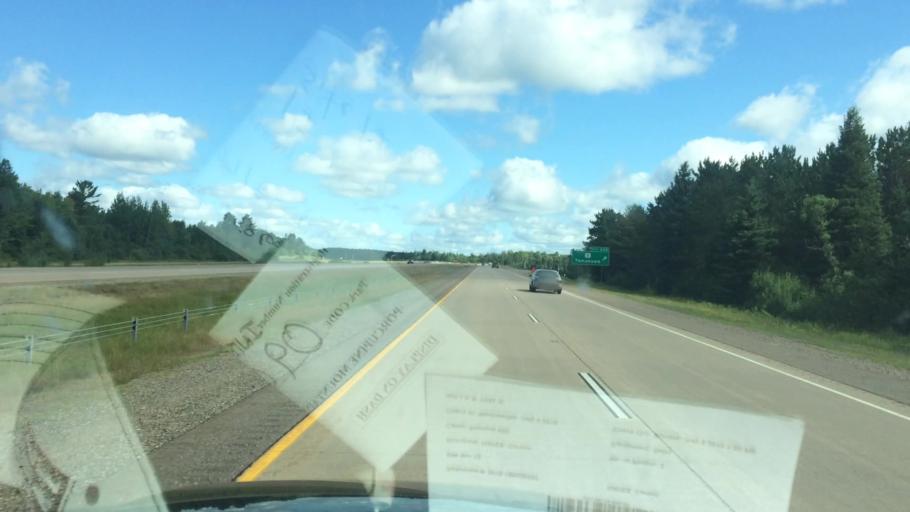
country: US
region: Wisconsin
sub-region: Lincoln County
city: Tomahawk
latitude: 45.4112
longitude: -89.6715
